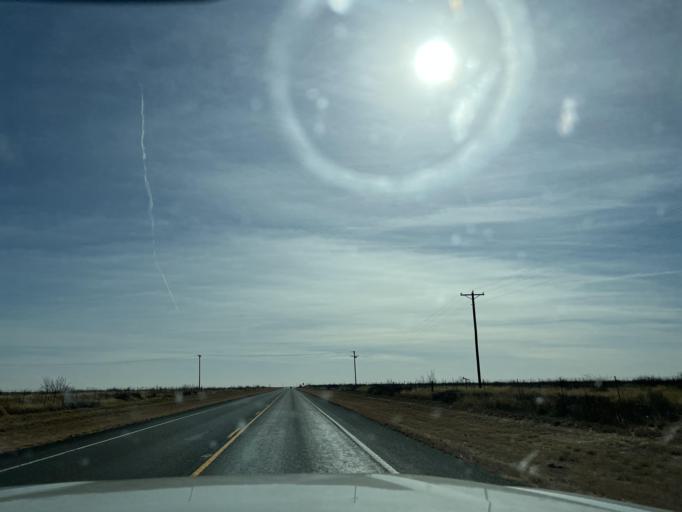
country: US
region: Texas
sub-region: Andrews County
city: Andrews
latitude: 32.4085
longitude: -102.4289
